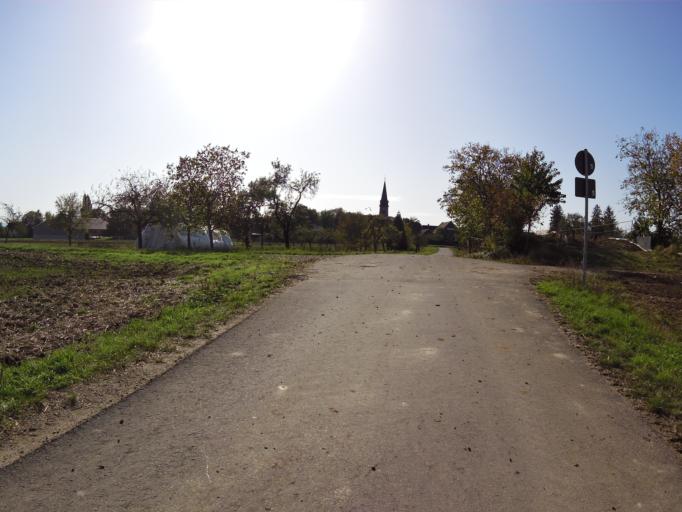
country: DE
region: Bavaria
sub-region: Regierungsbezirk Unterfranken
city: Biebelried
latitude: 49.7478
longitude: 10.0623
